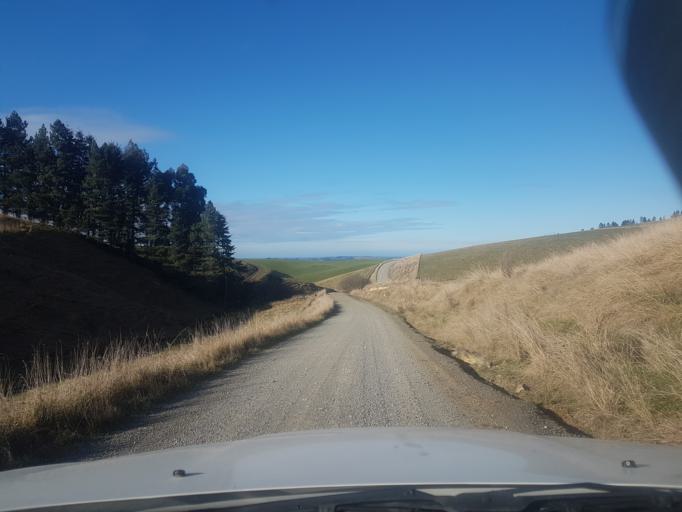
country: NZ
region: Canterbury
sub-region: Timaru District
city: Pleasant Point
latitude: -44.1661
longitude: 170.8969
